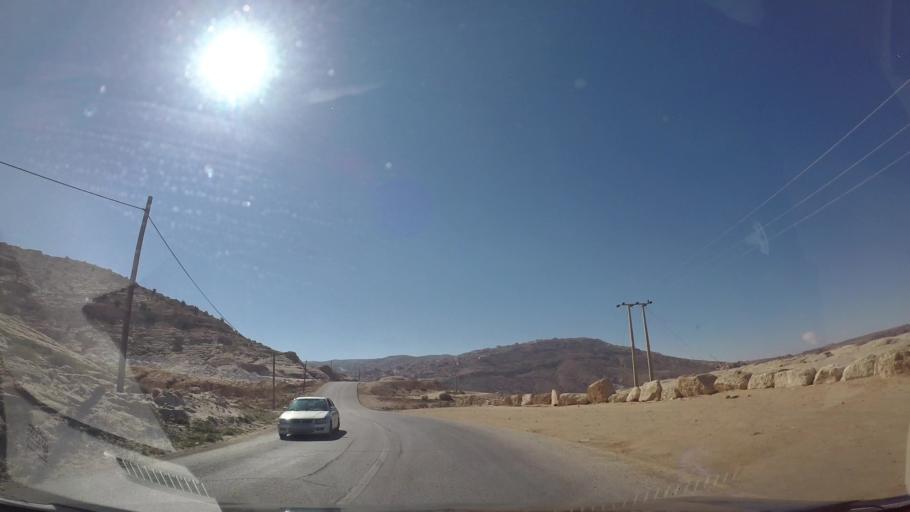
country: JO
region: Ma'an
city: Petra
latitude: 30.3323
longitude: 35.4681
